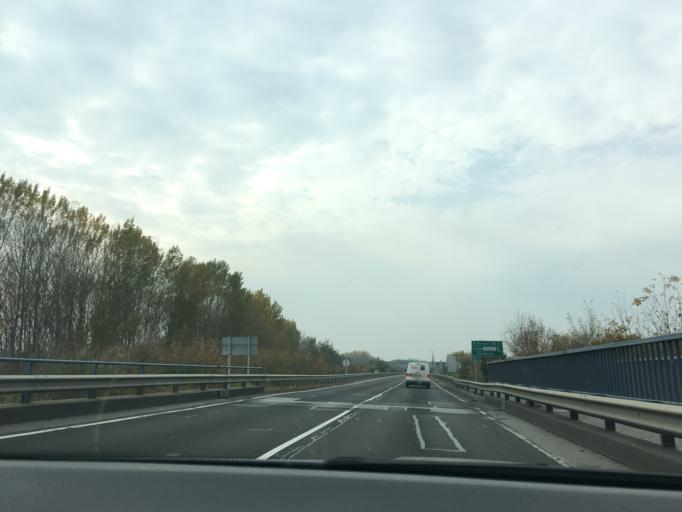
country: HU
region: Jasz-Nagykun-Szolnok
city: Szolnok
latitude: 47.1446
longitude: 20.1711
